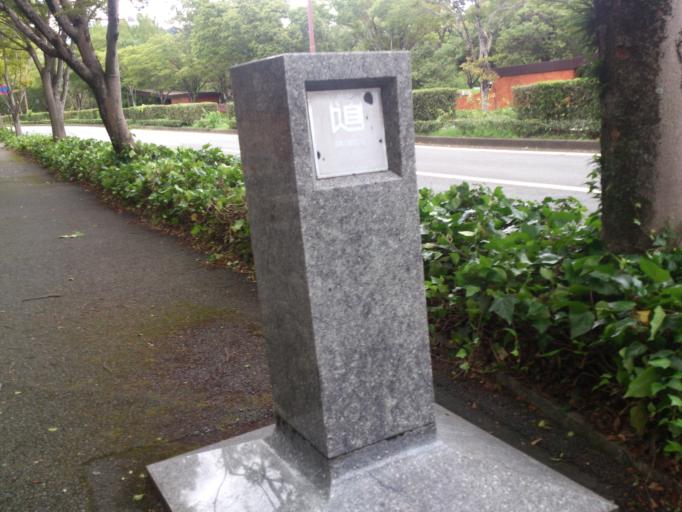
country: JP
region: Yamaguchi
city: Yamaguchi-shi
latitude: 34.1804
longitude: 131.4750
